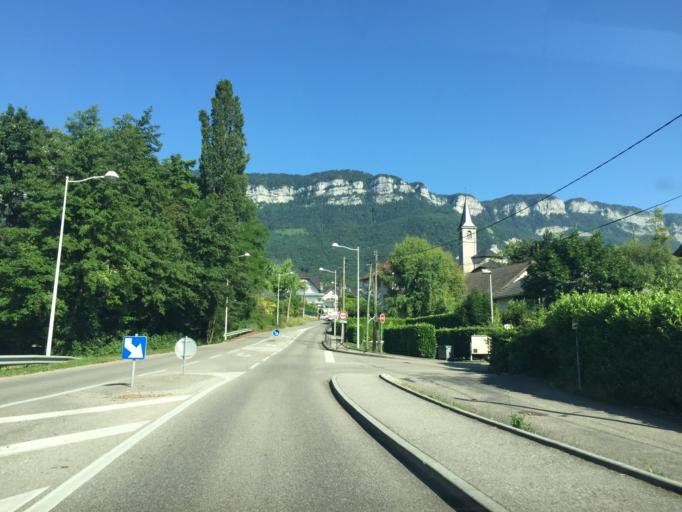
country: FR
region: Rhone-Alpes
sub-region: Departement de la Savoie
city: Mouxy
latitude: 45.6839
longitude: 5.9332
